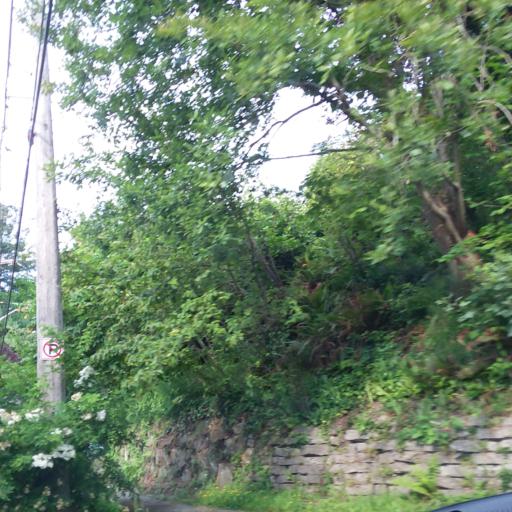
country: US
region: Washington
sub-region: King County
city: Seattle
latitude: 47.5790
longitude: -122.4031
